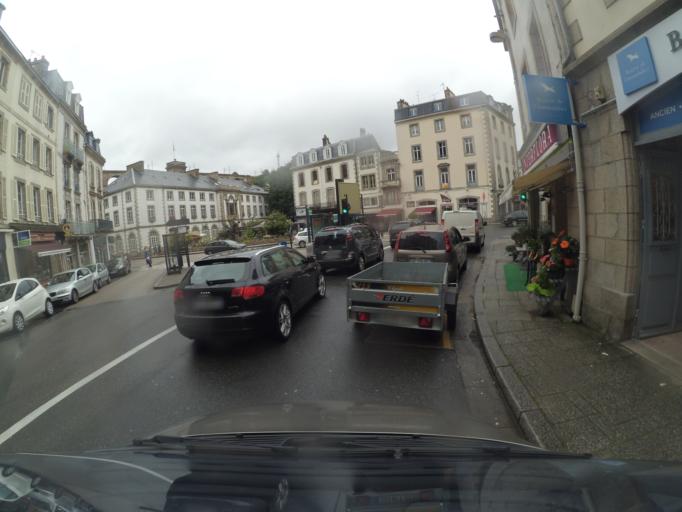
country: FR
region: Brittany
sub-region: Departement du Finistere
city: Morlaix
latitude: 48.5769
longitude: -3.8284
